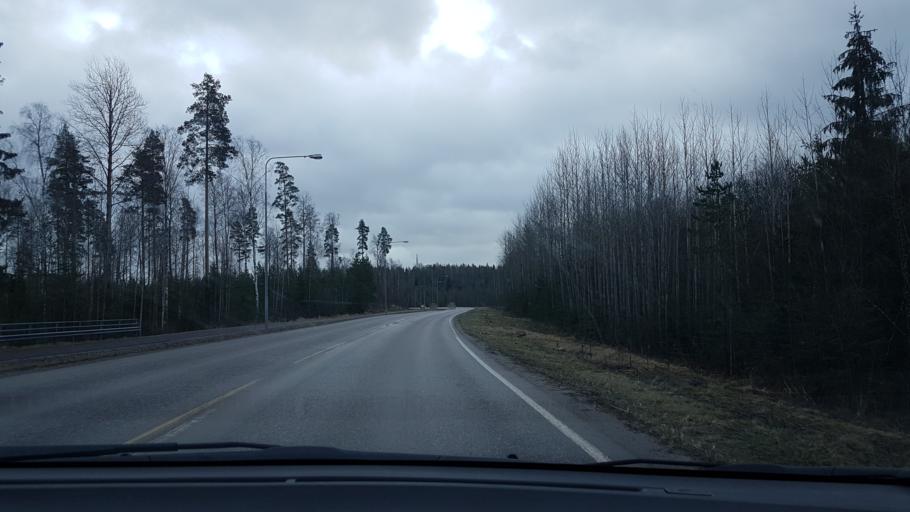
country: FI
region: Uusimaa
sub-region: Helsinki
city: Tuusula
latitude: 60.3742
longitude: 25.0605
